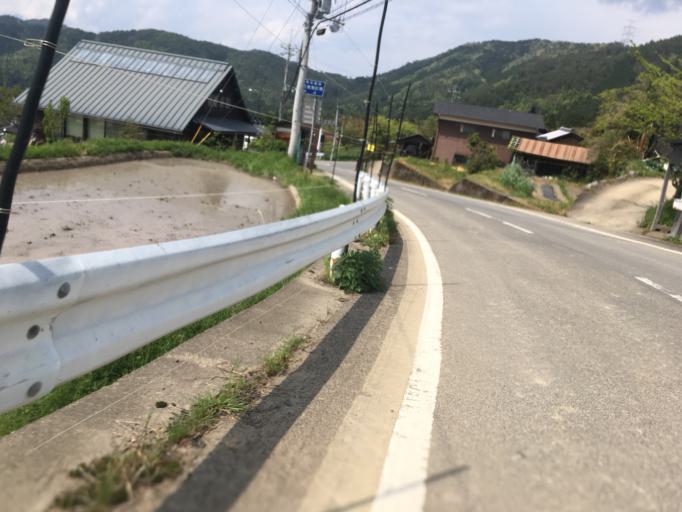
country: JP
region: Kyoto
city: Kameoka
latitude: 35.0841
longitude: 135.6109
